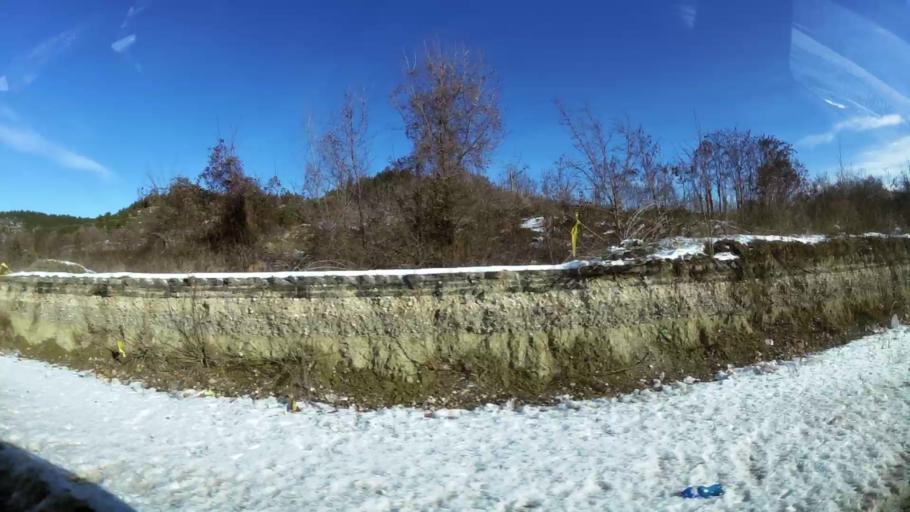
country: MK
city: Ljubin
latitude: 41.9858
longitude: 21.3026
